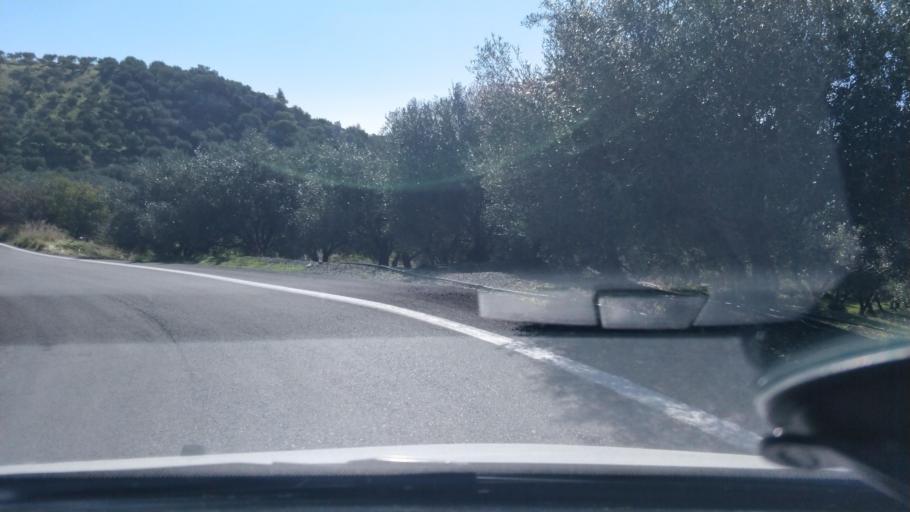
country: GR
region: Crete
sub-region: Nomos Irakleiou
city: Arkalochori
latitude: 35.0066
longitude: 25.4399
